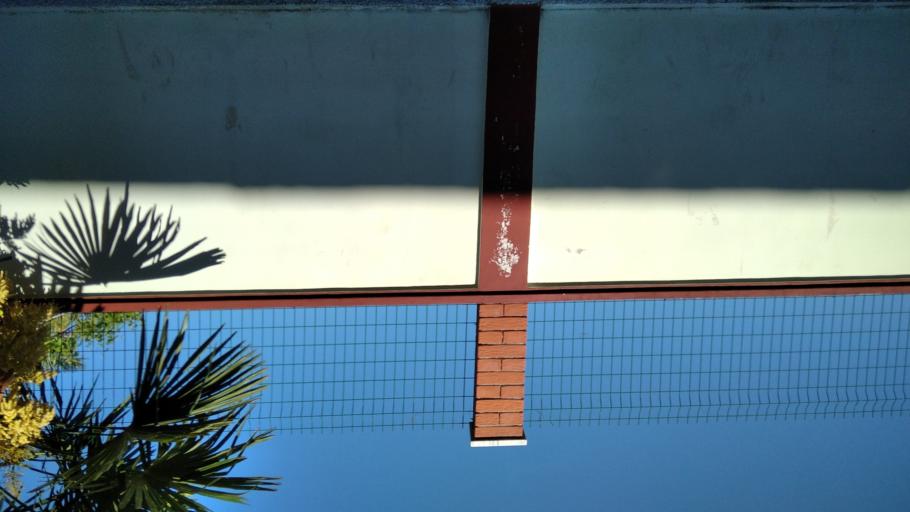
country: AL
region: Shkoder
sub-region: Rrethi i Shkodres
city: Shkoder
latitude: 42.0755
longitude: 19.5011
